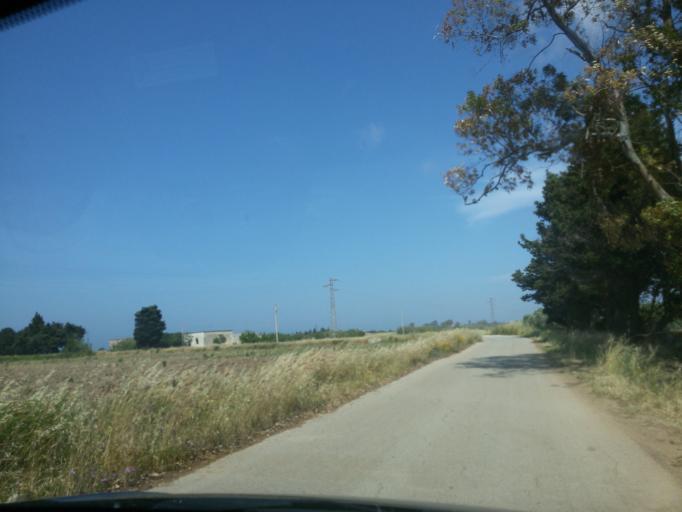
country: IT
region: Apulia
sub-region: Provincia di Brindisi
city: Brindisi
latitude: 40.6613
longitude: 17.8595
